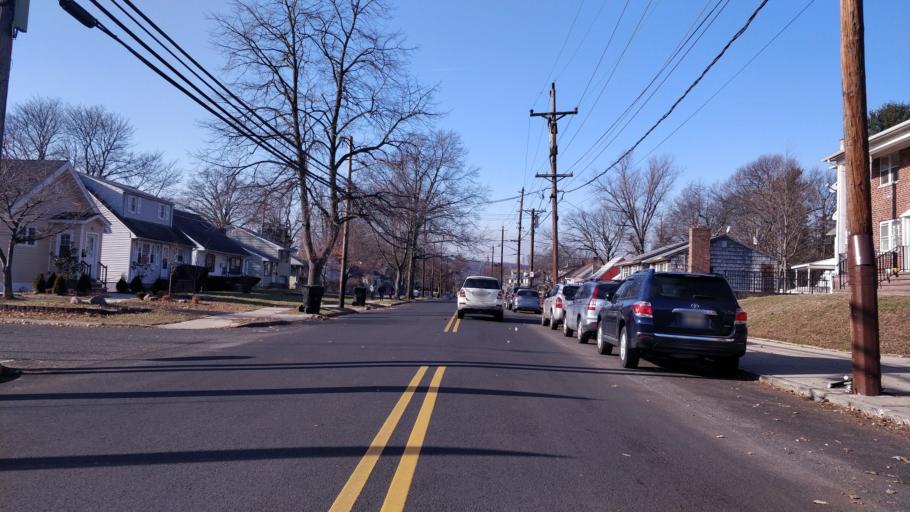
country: US
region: New Jersey
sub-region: Middlesex County
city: South Plainfield
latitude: 40.5975
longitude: -74.4381
